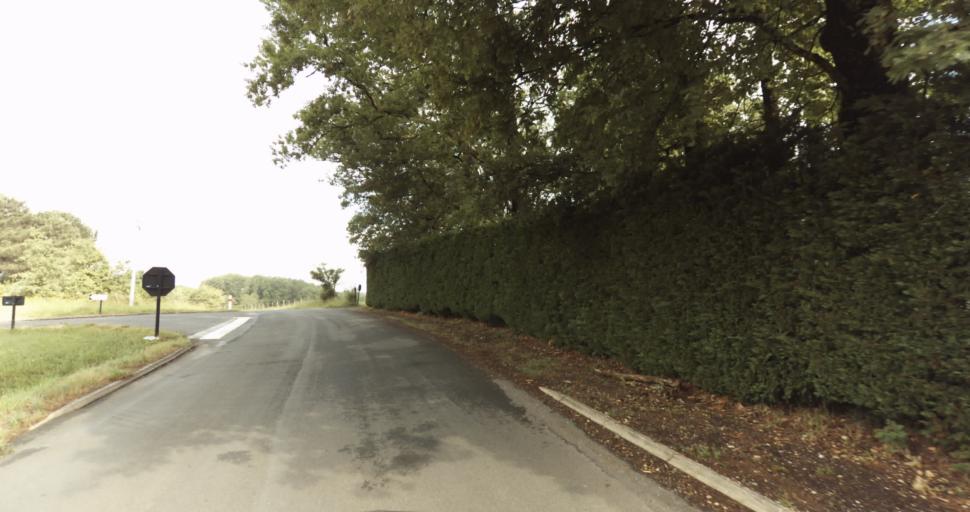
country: FR
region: Aquitaine
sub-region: Departement de la Dordogne
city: Le Bugue
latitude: 44.9403
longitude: 0.8190
